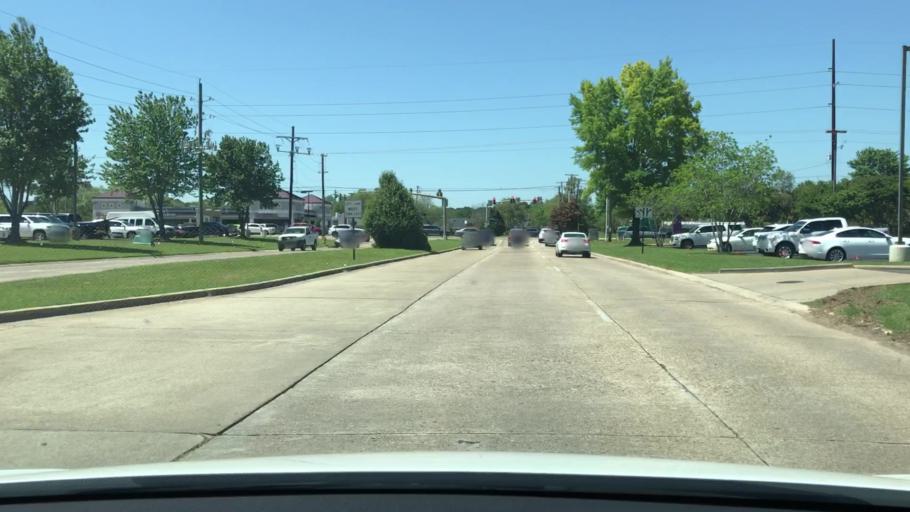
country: US
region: Louisiana
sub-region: Bossier Parish
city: Bossier City
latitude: 32.4269
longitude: -93.7166
